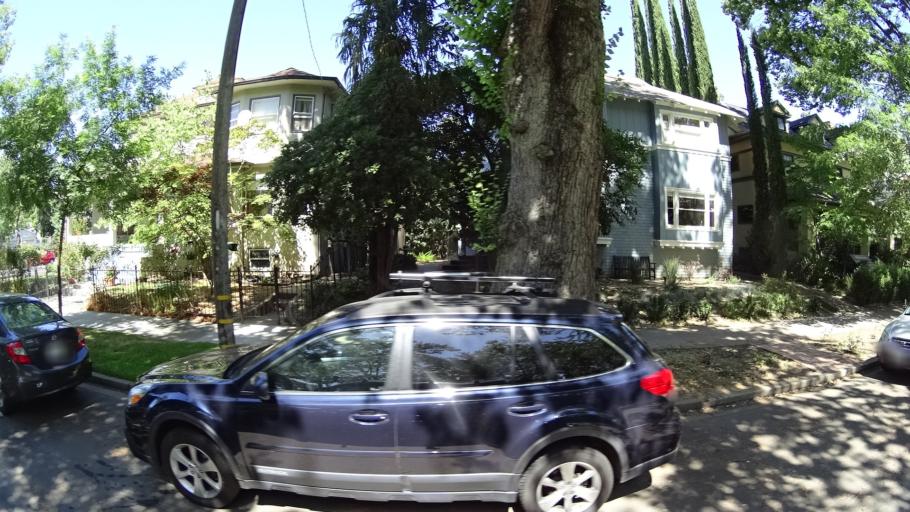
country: US
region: California
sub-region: Sacramento County
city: Sacramento
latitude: 38.5797
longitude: -121.4757
